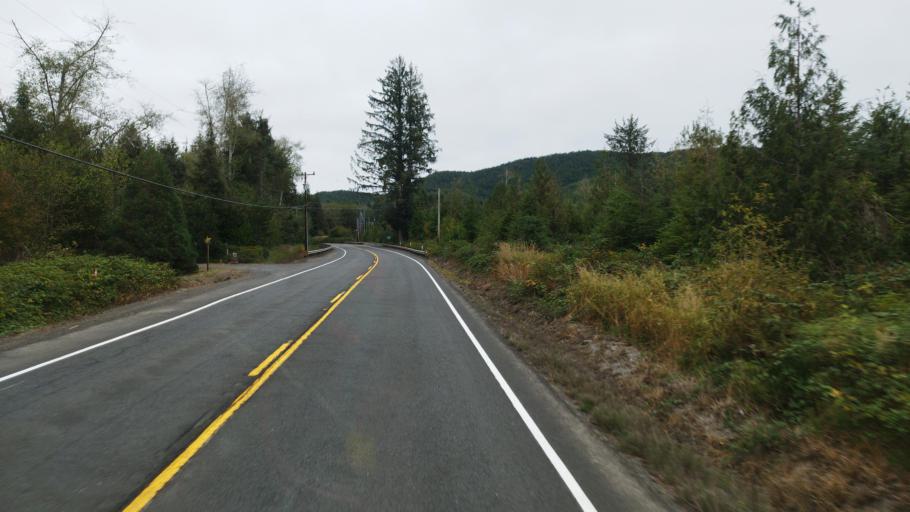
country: US
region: Oregon
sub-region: Clatsop County
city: Cannon Beach
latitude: 45.9022
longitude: -123.8704
